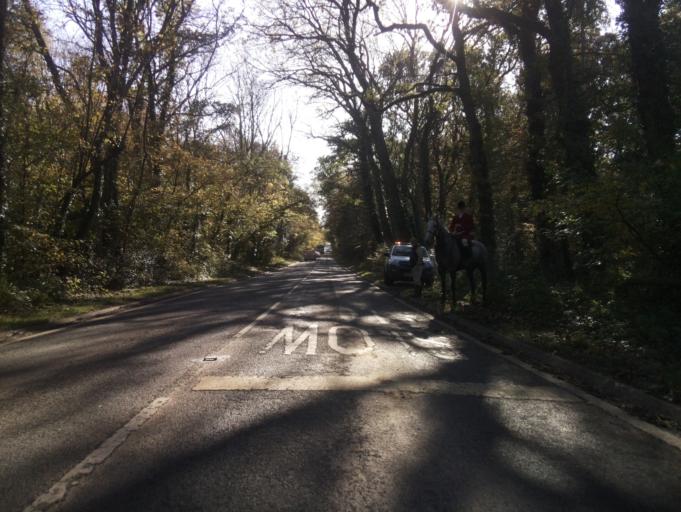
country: GB
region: England
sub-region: Dorset
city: Sherborne
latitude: 50.8970
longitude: -2.4934
